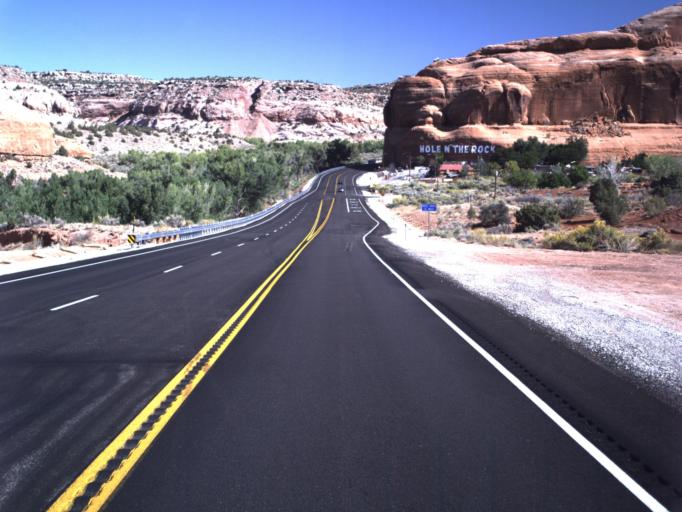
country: US
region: Utah
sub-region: Grand County
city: Moab
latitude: 38.3867
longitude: -109.4560
